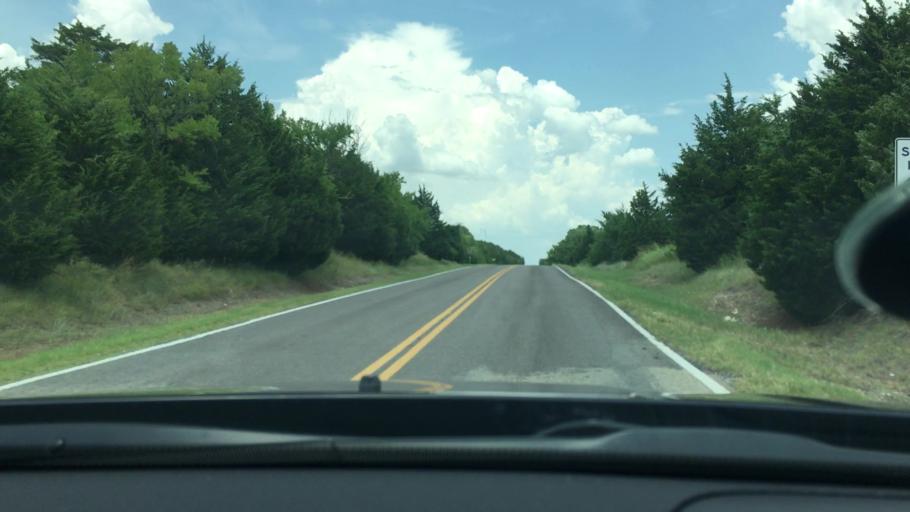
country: US
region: Oklahoma
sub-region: Marshall County
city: Oakland
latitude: 34.0003
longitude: -96.8808
